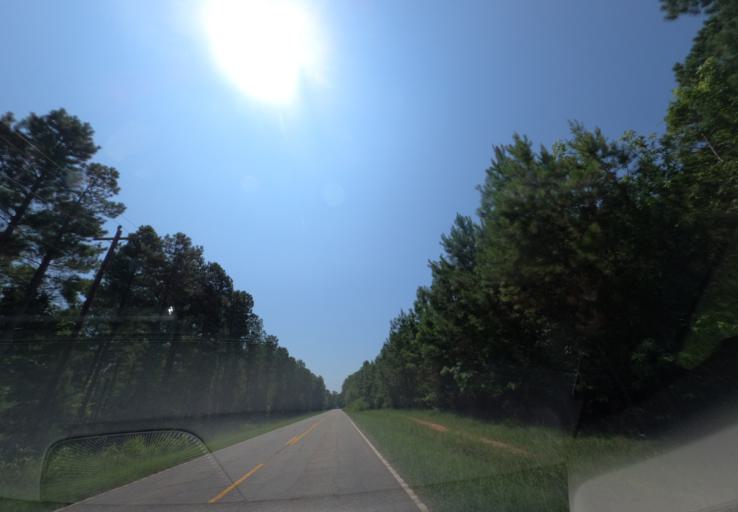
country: US
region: South Carolina
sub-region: Greenwood County
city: Greenwood
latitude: 34.0618
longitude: -82.1423
